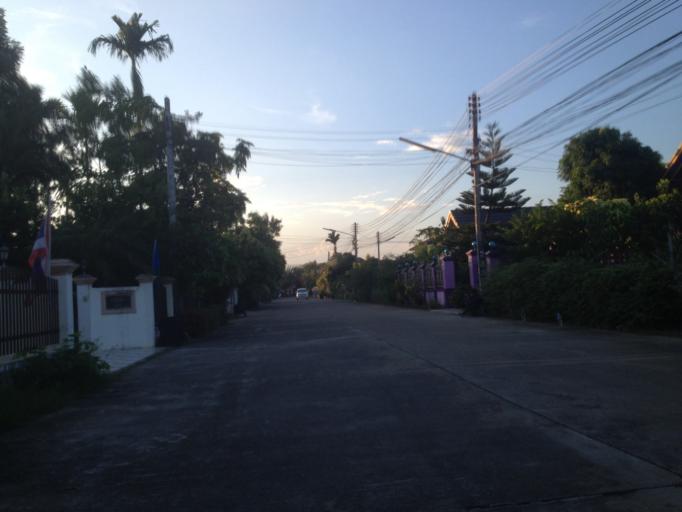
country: TH
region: Chiang Mai
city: Hang Dong
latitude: 18.6983
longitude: 98.9239
